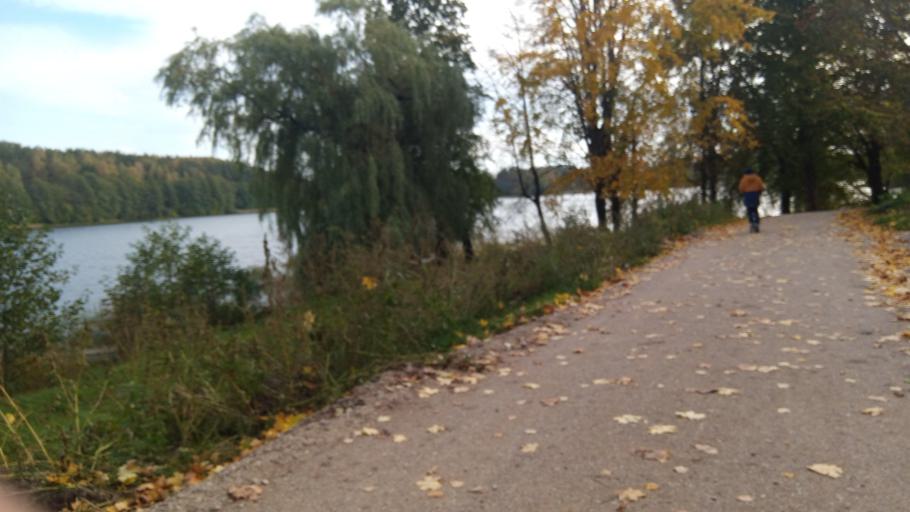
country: LT
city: Trakai
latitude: 54.6364
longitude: 24.9411
